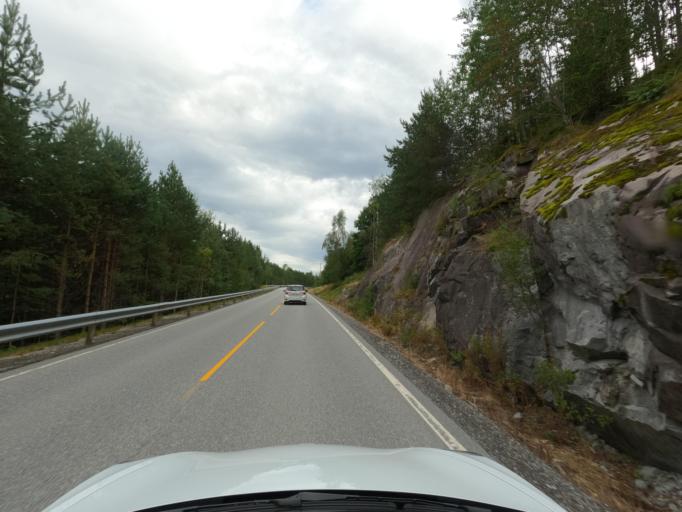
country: NO
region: Telemark
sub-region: Hjartdal
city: Sauland
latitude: 59.7494
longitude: 9.0190
